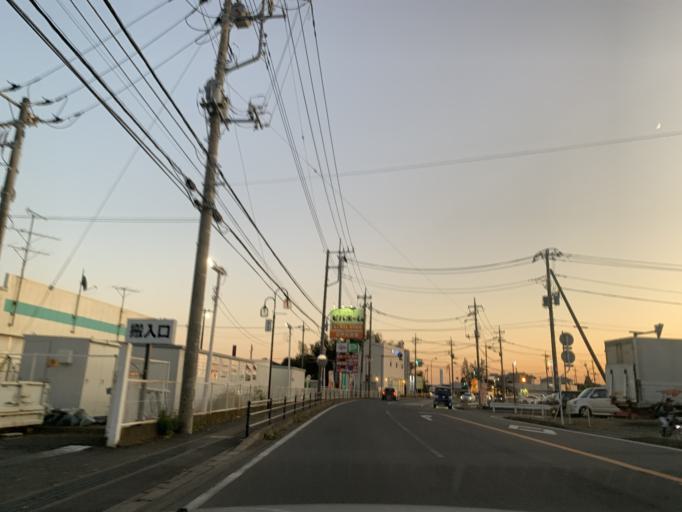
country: JP
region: Chiba
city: Nagareyama
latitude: 35.8973
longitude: 139.9027
